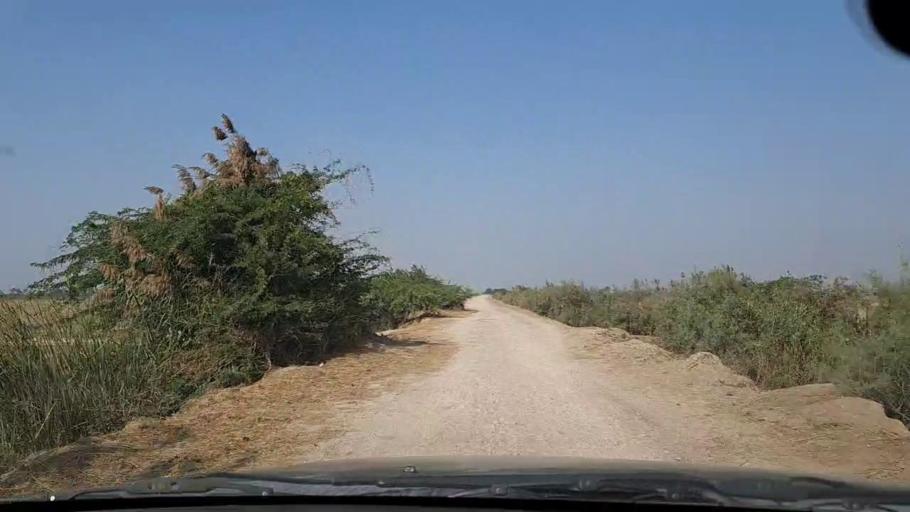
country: PK
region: Sindh
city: Mirpur Sakro
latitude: 24.3533
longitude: 67.6831
